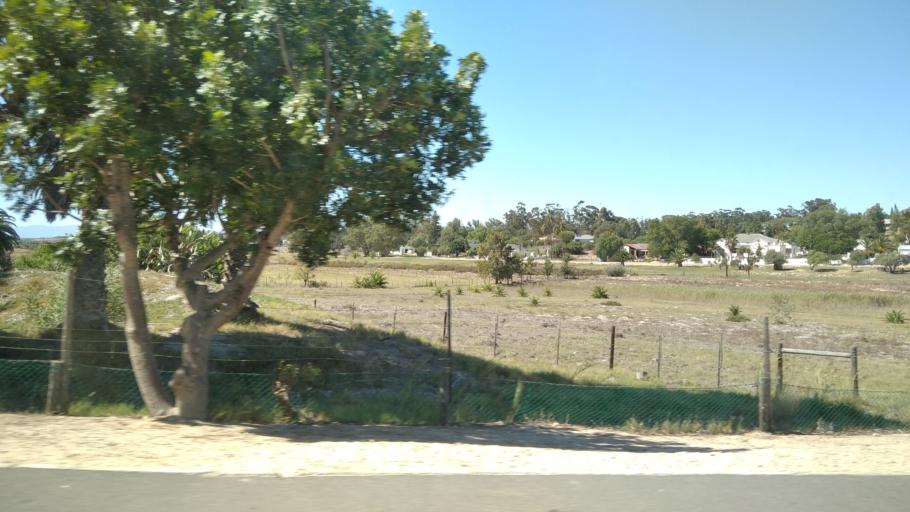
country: ZA
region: Western Cape
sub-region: West Coast District Municipality
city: Moorreesburg
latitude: -33.0614
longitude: 18.3435
